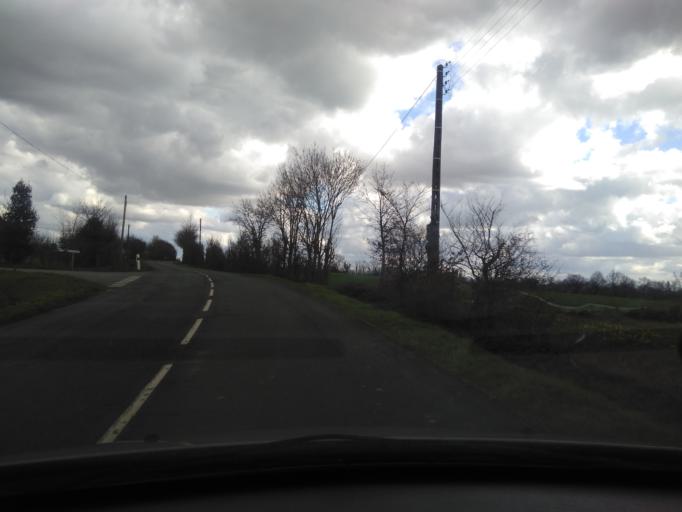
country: FR
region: Pays de la Loire
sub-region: Departement de la Vendee
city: Saint-Martin-des-Noyers
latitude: 46.7442
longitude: -1.1936
